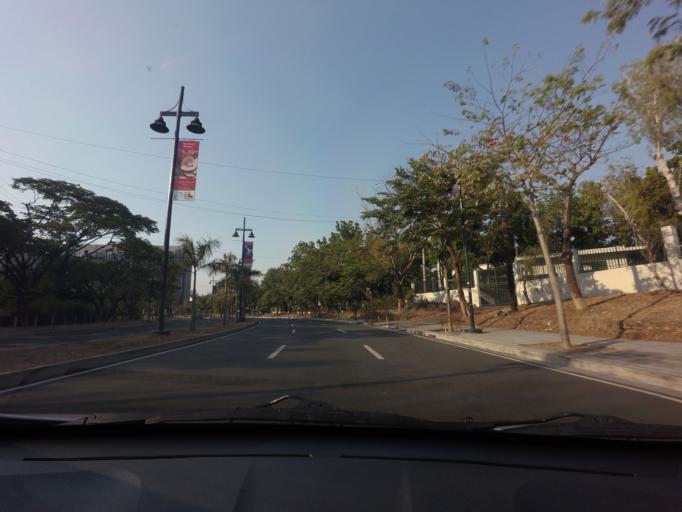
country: PH
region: Calabarzon
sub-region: Province of Rizal
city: Pateros
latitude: 14.5566
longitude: 121.0589
